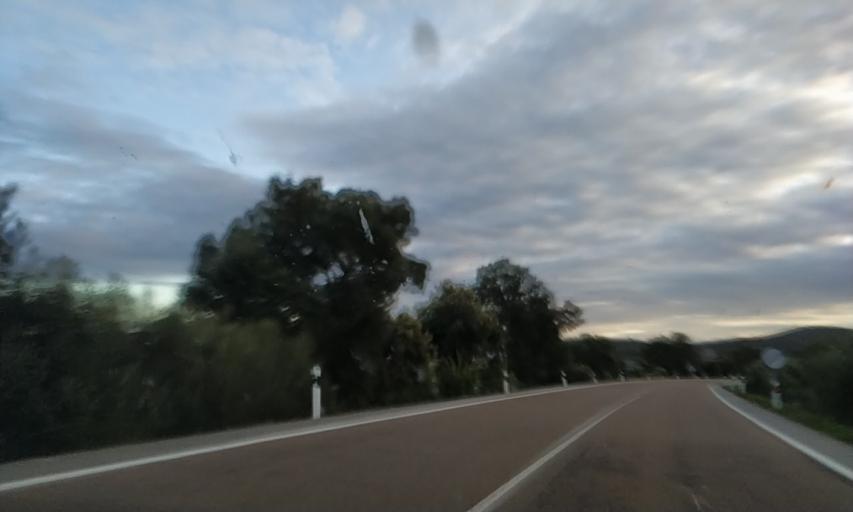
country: ES
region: Extremadura
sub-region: Provincia de Badajoz
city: Puebla de Obando
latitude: 39.2723
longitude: -6.5207
